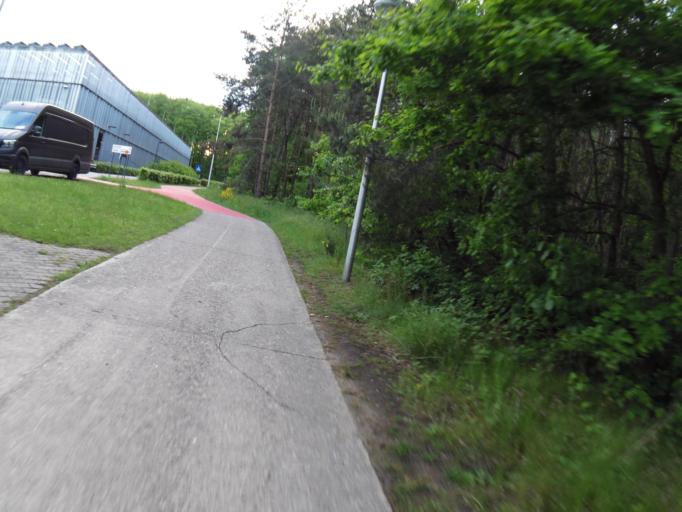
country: BE
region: Flanders
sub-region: Provincie Limburg
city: Genk
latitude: 50.9591
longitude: 5.5180
